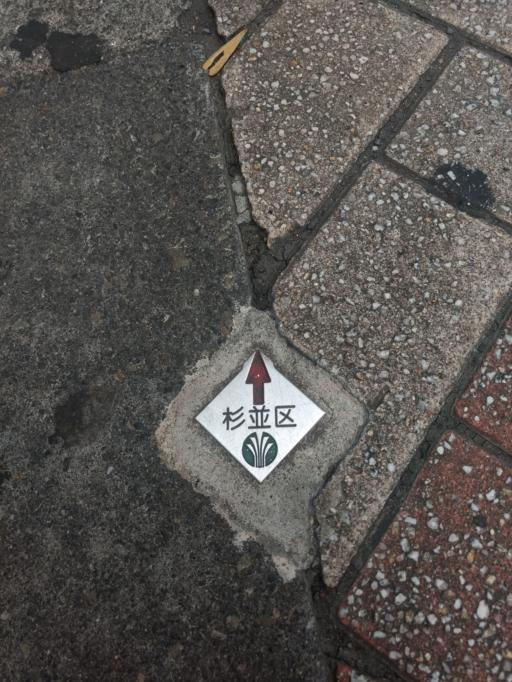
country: JP
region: Tokyo
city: Musashino
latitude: 35.7044
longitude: 139.6000
